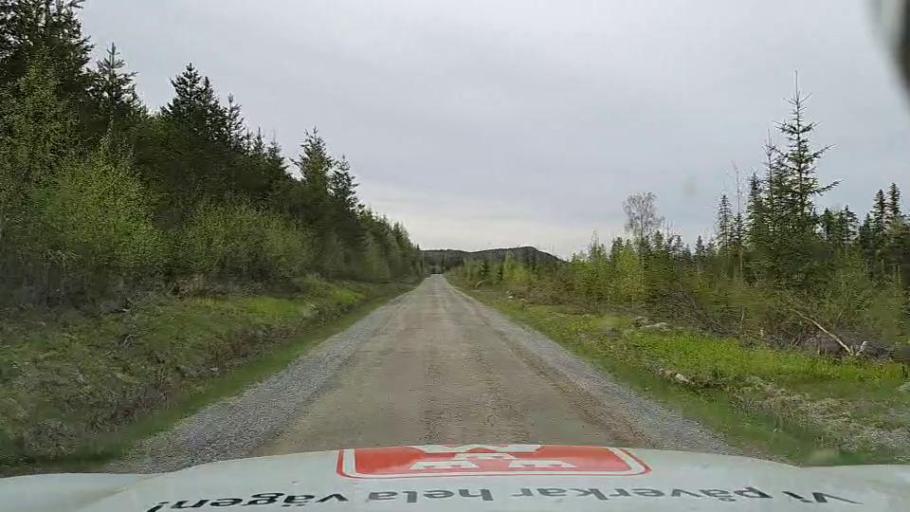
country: SE
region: Jaemtland
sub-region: Bergs Kommun
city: Hoverberg
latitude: 62.5396
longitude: 14.9052
